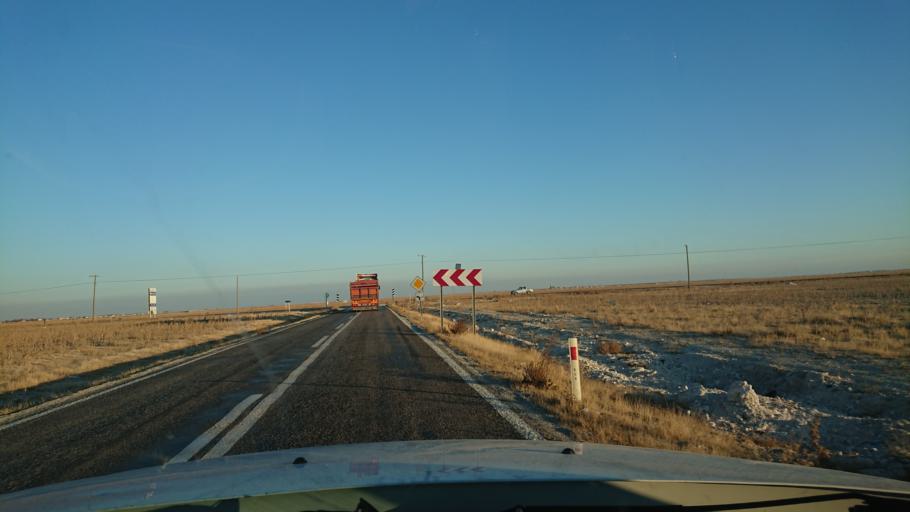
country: TR
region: Aksaray
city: Eskil
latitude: 38.3761
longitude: 33.3705
